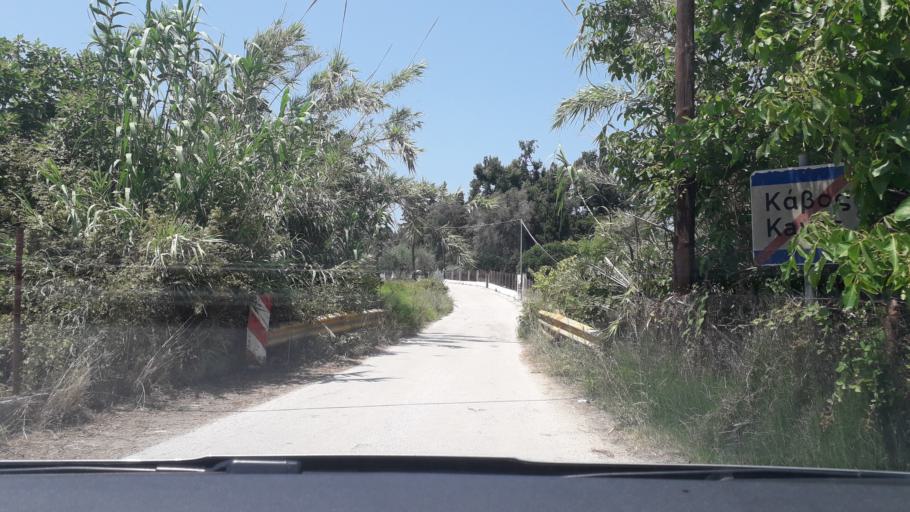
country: GR
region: Ionian Islands
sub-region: Nomos Kerkyras
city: Lefkimmi
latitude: 39.3784
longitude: 20.1133
